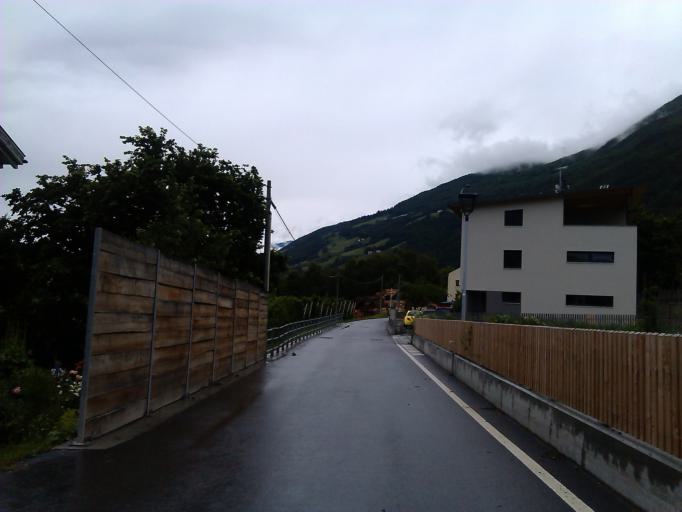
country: IT
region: Trentino-Alto Adige
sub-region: Bolzano
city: Lasa
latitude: 46.6144
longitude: 10.7033
